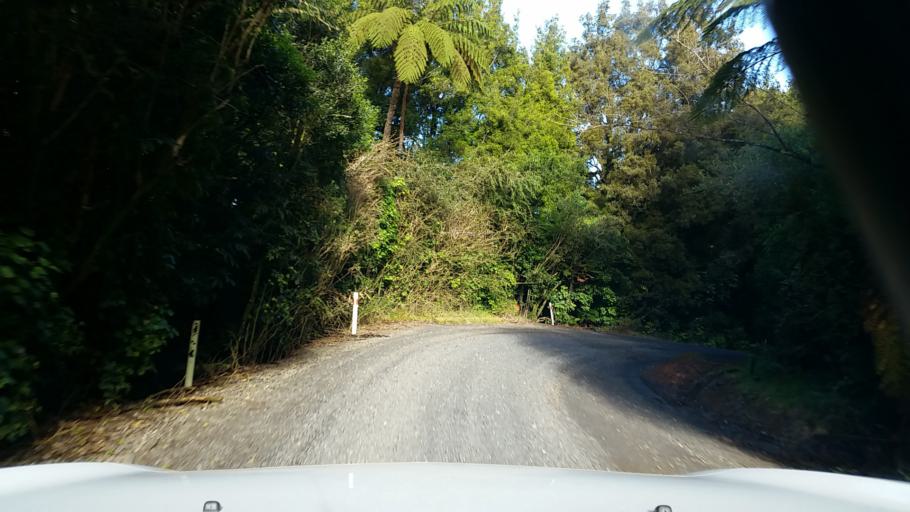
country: NZ
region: Waikato
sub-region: Matamata-Piako District
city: Matamata
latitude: -37.8163
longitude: 175.6325
